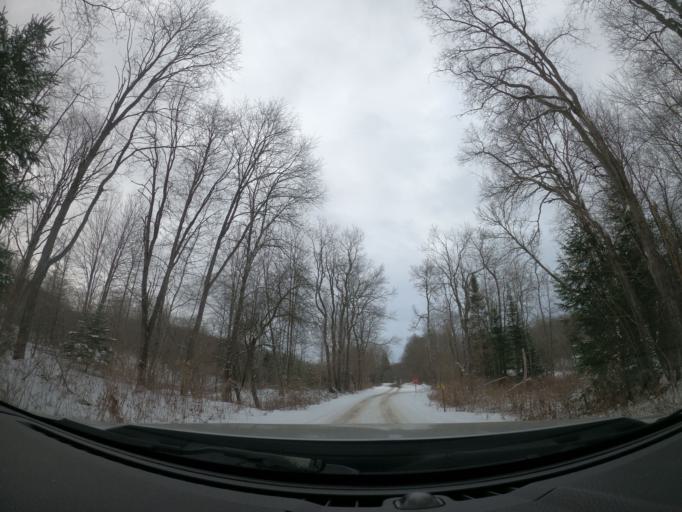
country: US
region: New York
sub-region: Cayuga County
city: Moravia
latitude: 42.7340
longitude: -76.2849
